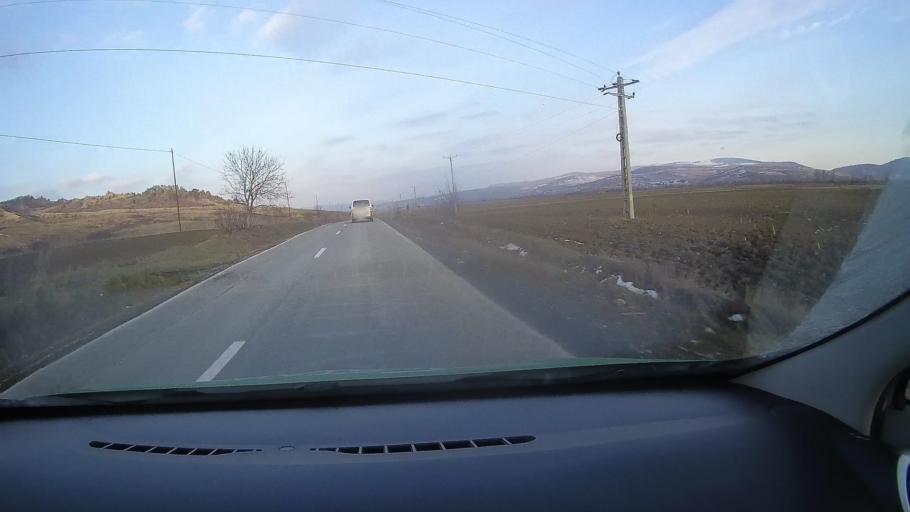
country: RO
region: Mures
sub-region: Comuna Vanatori
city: Vanatori
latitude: 46.2537
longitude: 24.9443
